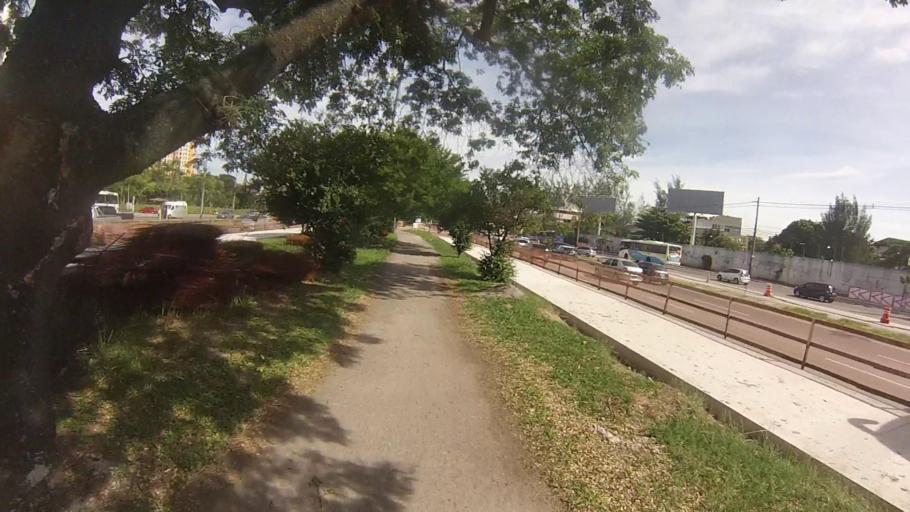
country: BR
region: Rio de Janeiro
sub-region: Rio De Janeiro
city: Rio de Janeiro
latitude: -23.0003
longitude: -43.3386
